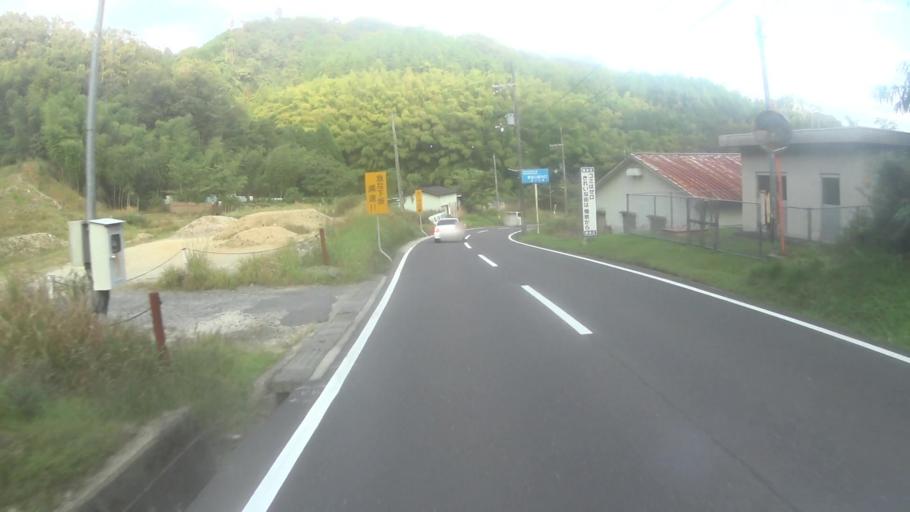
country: JP
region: Kyoto
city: Miyazu
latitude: 35.5418
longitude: 135.0857
